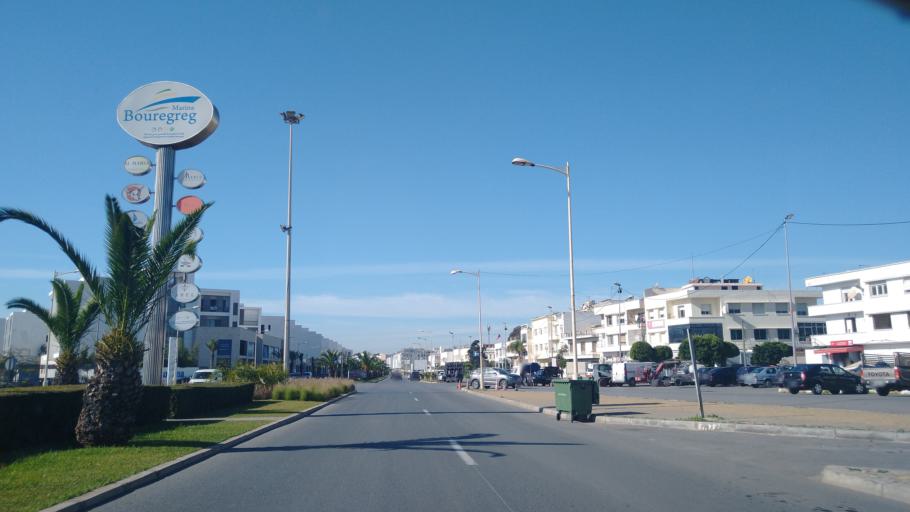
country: MA
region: Rabat-Sale-Zemmour-Zaer
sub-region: Rabat
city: Rabat
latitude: 34.0319
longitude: -6.8216
